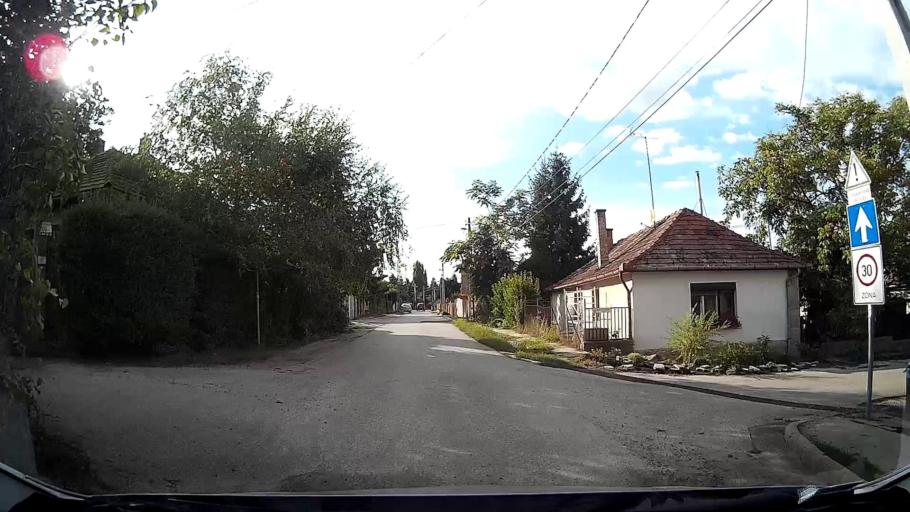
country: HU
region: Pest
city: Pomaz
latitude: 47.6407
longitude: 19.0243
